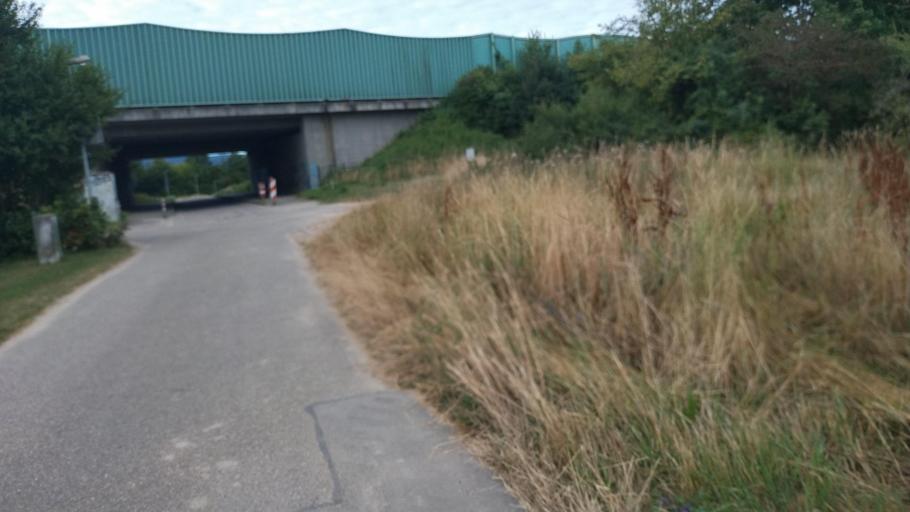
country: DE
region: Baden-Wuerttemberg
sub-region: Karlsruhe Region
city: Ettlingen
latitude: 48.9591
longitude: 8.3925
